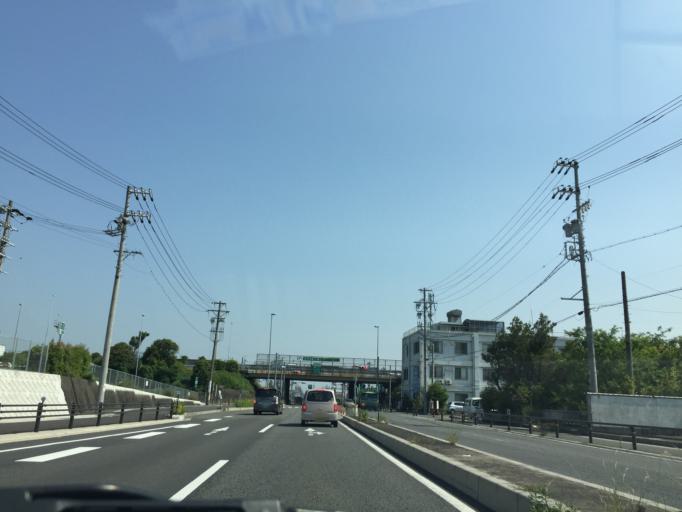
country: JP
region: Gifu
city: Ogaki
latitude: 35.3152
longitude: 136.6176
